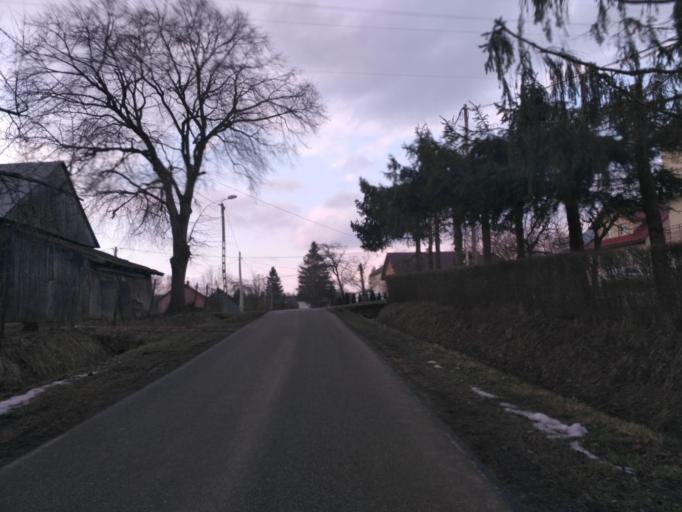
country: PL
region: Subcarpathian Voivodeship
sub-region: Powiat sanocki
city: Strachocina
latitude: 49.6106
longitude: 22.0824
